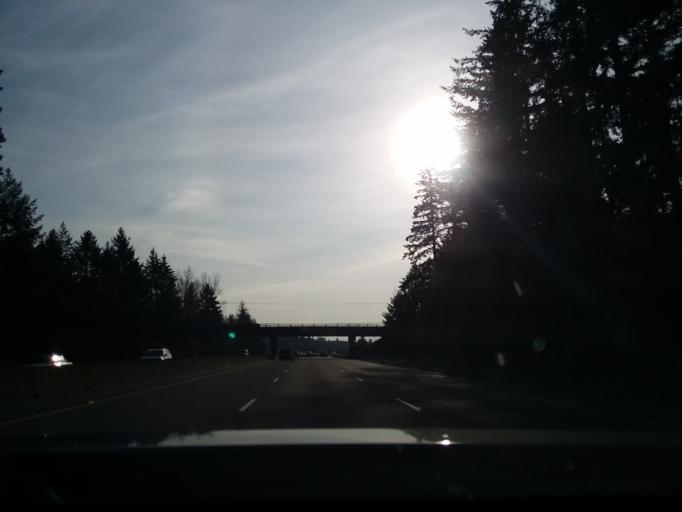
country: US
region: Washington
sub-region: Thurston County
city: Tumwater
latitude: 46.9247
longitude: -122.9459
